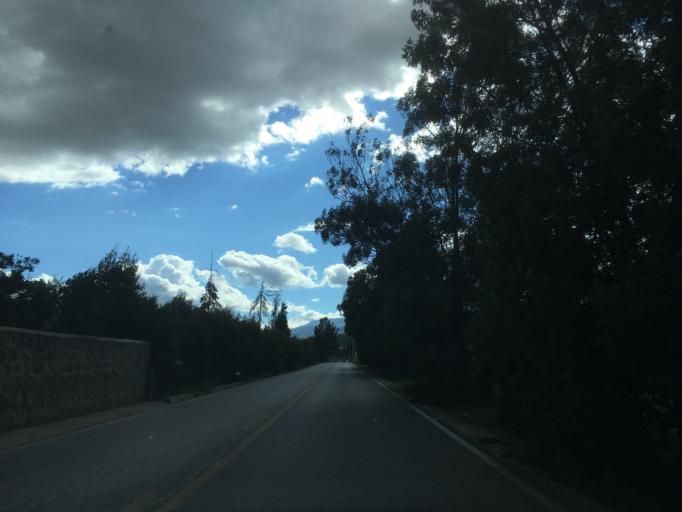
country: CO
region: Boyaca
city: Firavitoba
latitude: 5.6350
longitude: -72.9996
